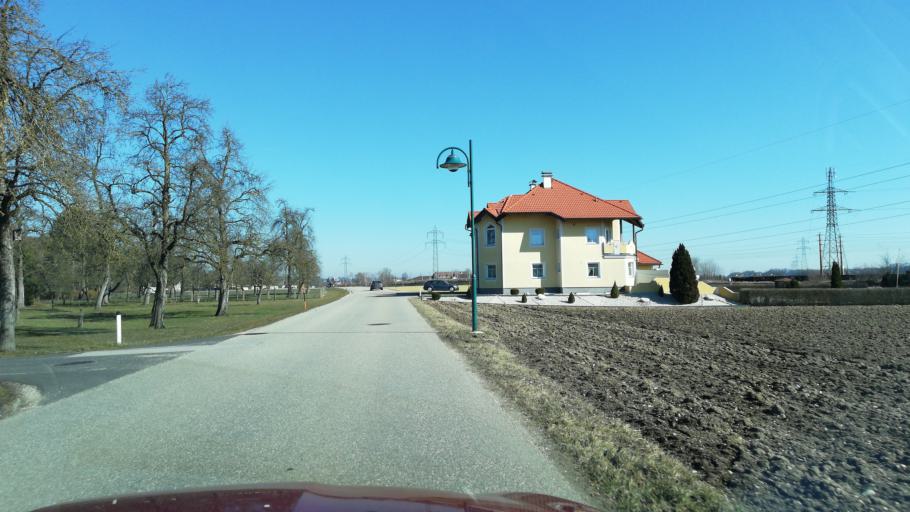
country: AT
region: Upper Austria
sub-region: Politischer Bezirk Vocklabruck
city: Redlham
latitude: 48.0290
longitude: 13.7342
